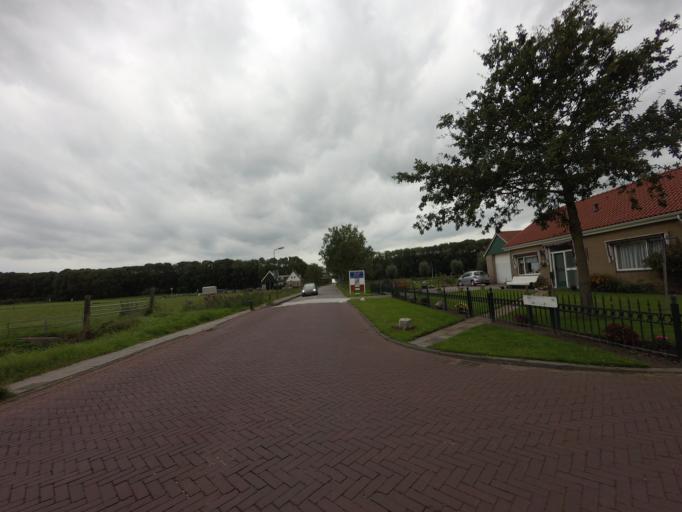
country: NL
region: Friesland
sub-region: Sudwest Fryslan
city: Bolsward
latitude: 53.0488
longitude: 5.5755
